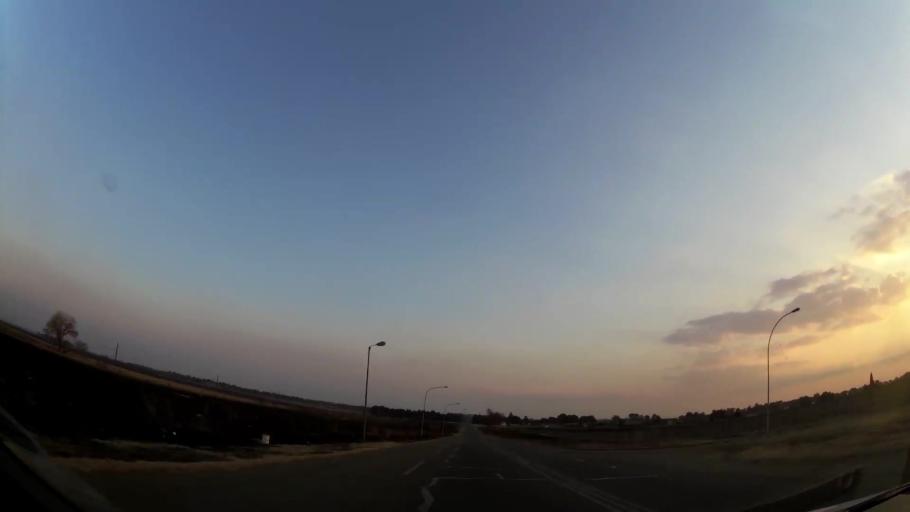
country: ZA
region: Gauteng
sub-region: Ekurhuleni Metropolitan Municipality
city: Springs
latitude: -26.3294
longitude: 28.4433
